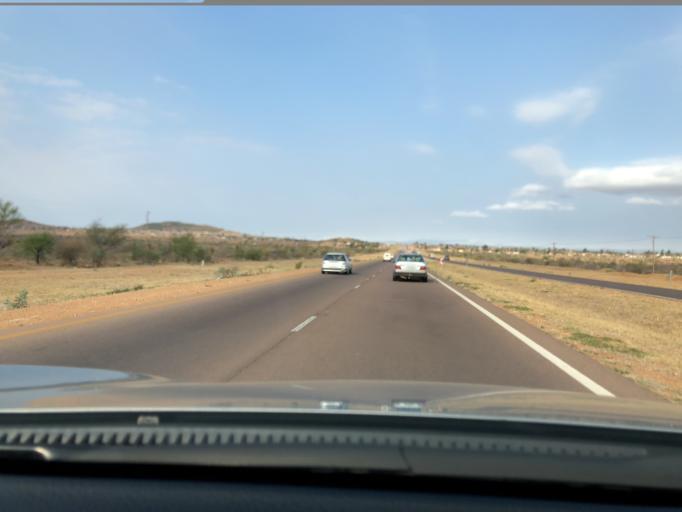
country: ZA
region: Limpopo
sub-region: Capricorn District Municipality
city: Polokwane
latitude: -23.8942
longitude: 29.6393
